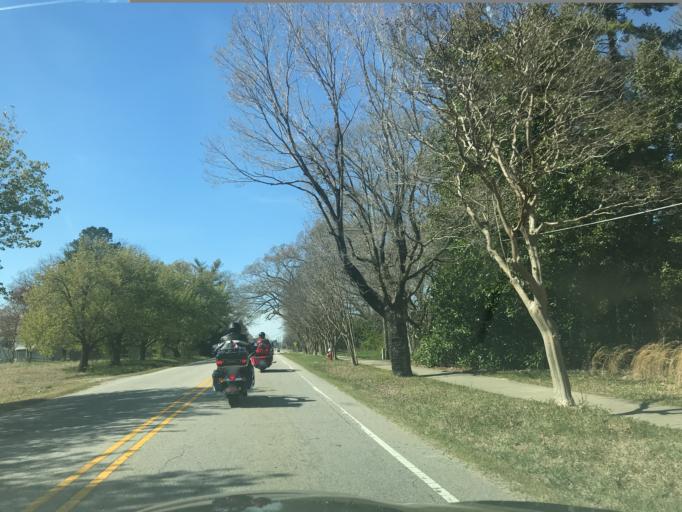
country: US
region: North Carolina
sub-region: Wake County
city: Fuquay-Varina
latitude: 35.5951
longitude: -78.7968
